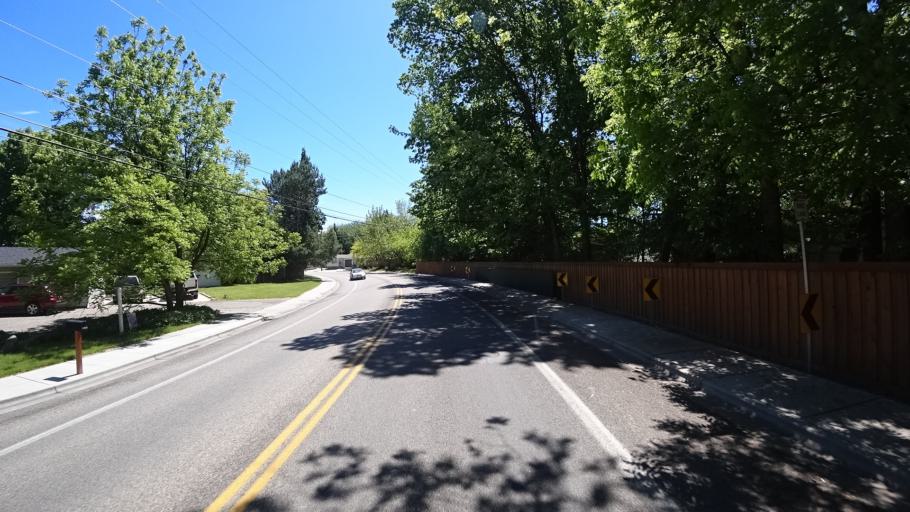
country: US
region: Idaho
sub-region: Ada County
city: Boise
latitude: 43.5645
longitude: -116.1447
